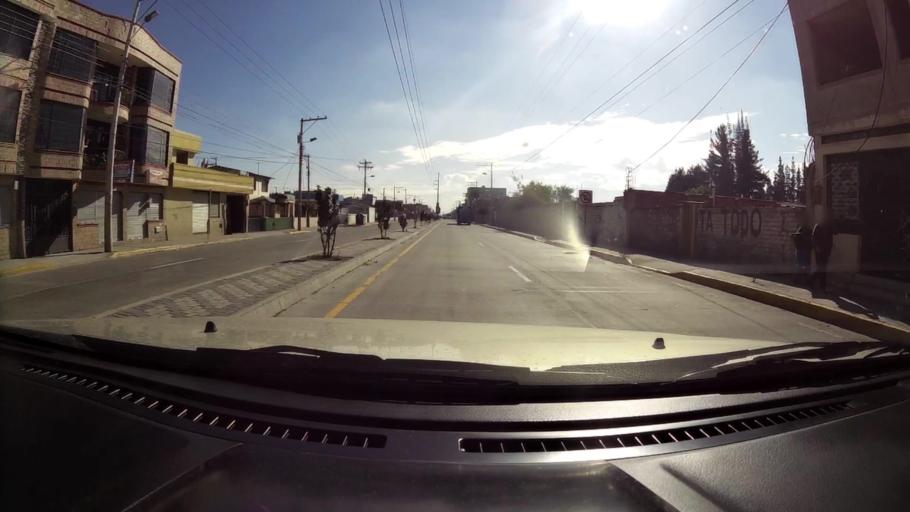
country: EC
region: Chimborazo
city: Riobamba
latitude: -1.6461
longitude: -78.6797
